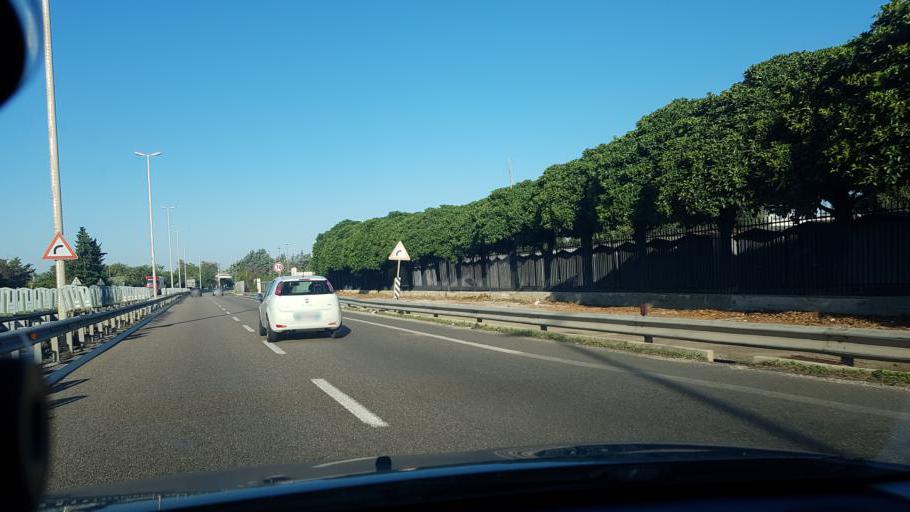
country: IT
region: Apulia
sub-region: Provincia di Bari
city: Parco Scizzo-Parchitello
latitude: 41.0838
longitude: 16.9969
